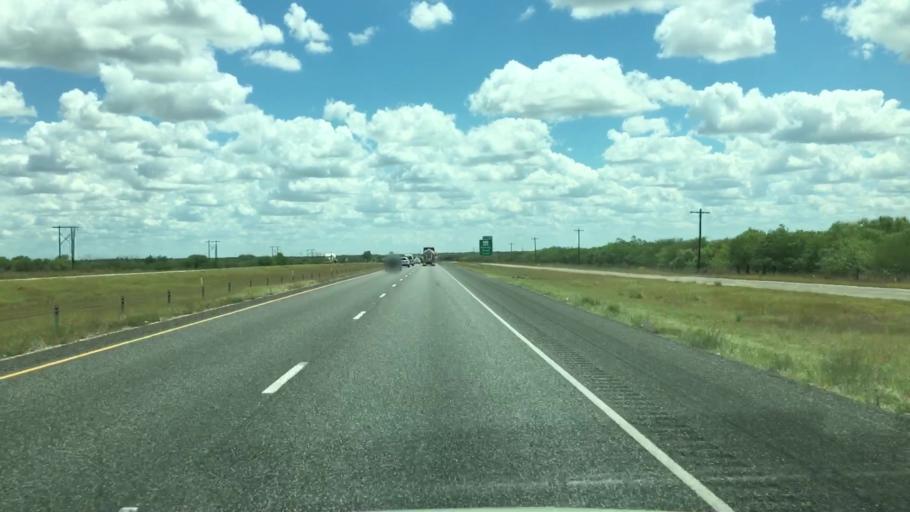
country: US
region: Texas
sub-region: Atascosa County
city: Pleasanton
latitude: 28.8609
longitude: -98.3878
